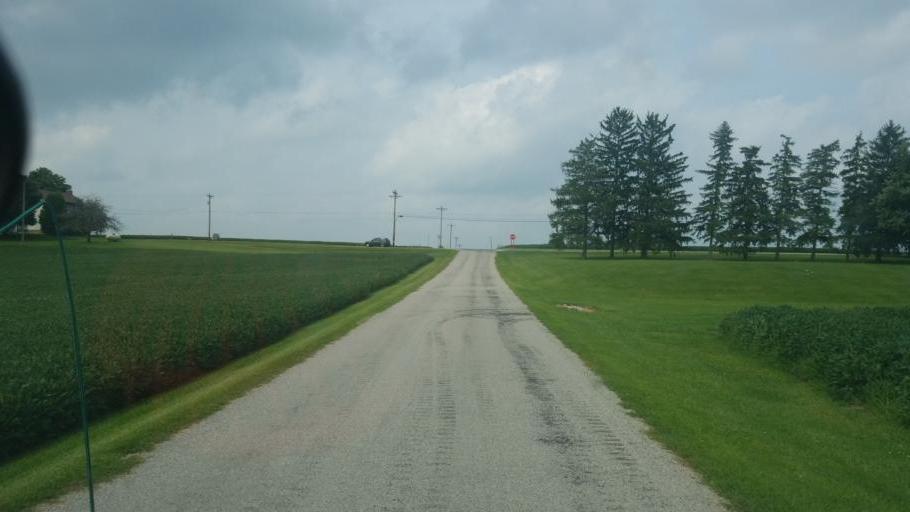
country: US
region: Ohio
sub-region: Huron County
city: New London
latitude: 41.0890
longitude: -82.4622
